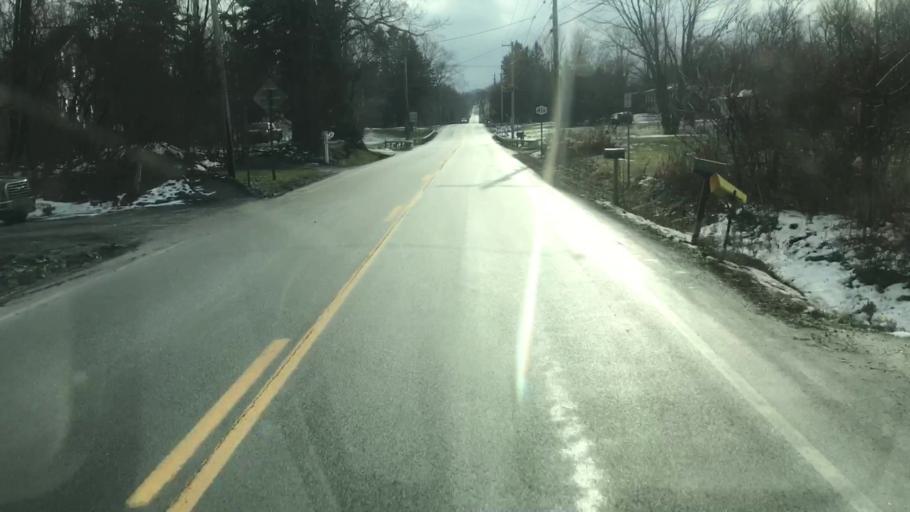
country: US
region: New York
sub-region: Onondaga County
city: Skaneateles
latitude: 42.8643
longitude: -76.4023
